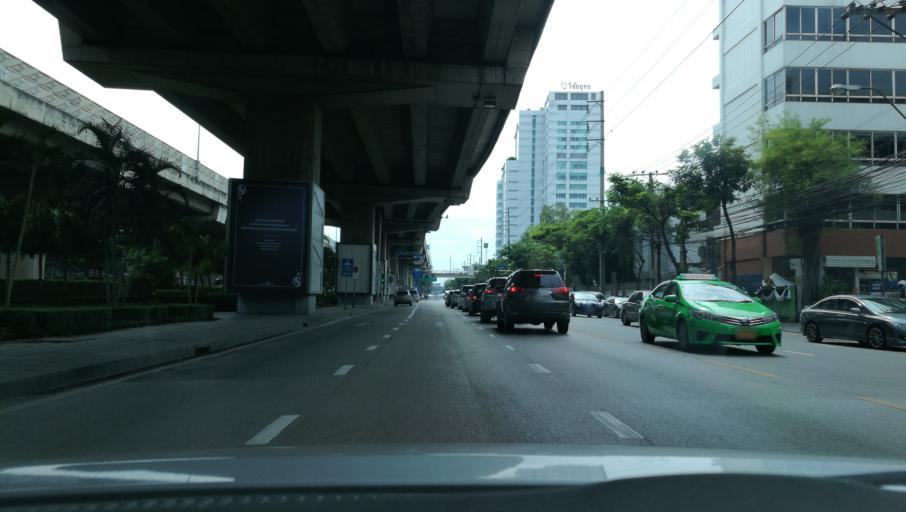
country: TH
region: Bangkok
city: Phaya Thai
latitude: 13.7834
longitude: 100.5344
